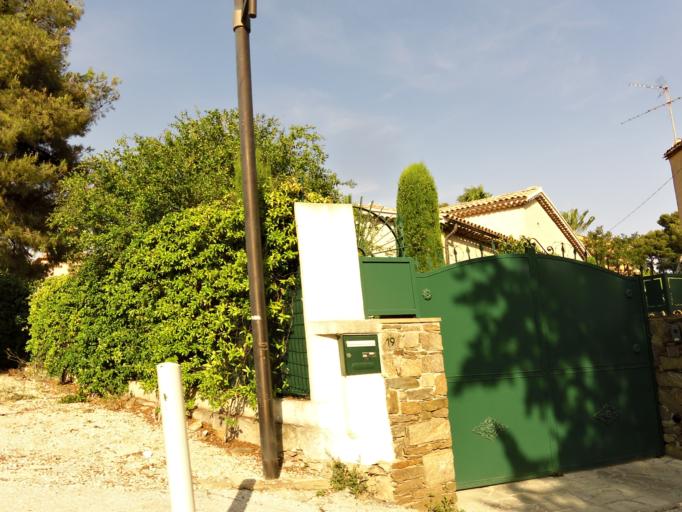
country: FR
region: Provence-Alpes-Cote d'Azur
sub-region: Departement du Var
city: Carqueiranne
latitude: 43.0858
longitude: 6.0708
